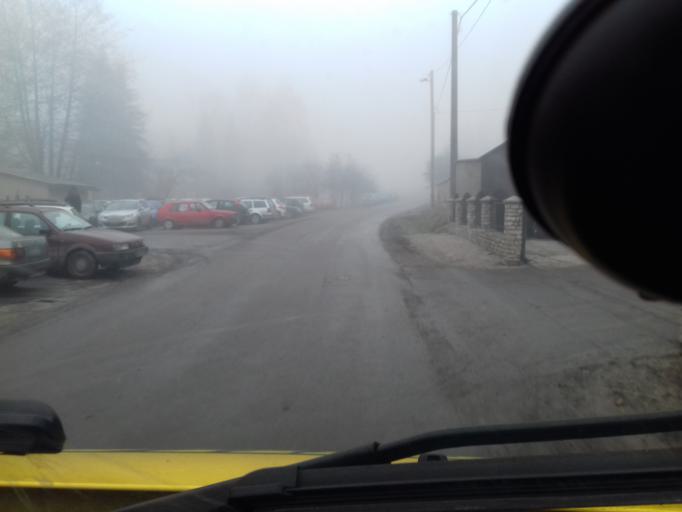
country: BA
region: Federation of Bosnia and Herzegovina
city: Lokvine
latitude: 44.2263
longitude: 17.8555
